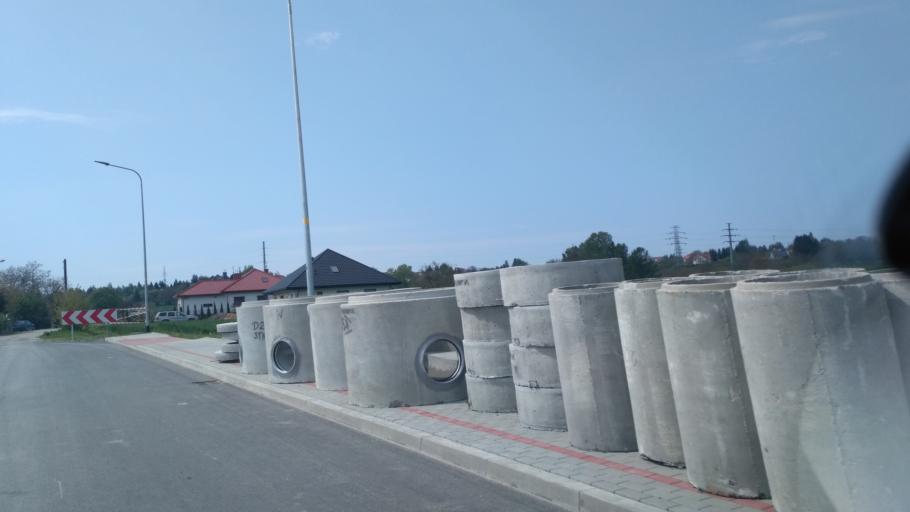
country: PL
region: Subcarpathian Voivodeship
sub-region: Powiat jaroslawski
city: Jaroslaw
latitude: 50.0017
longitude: 22.6805
